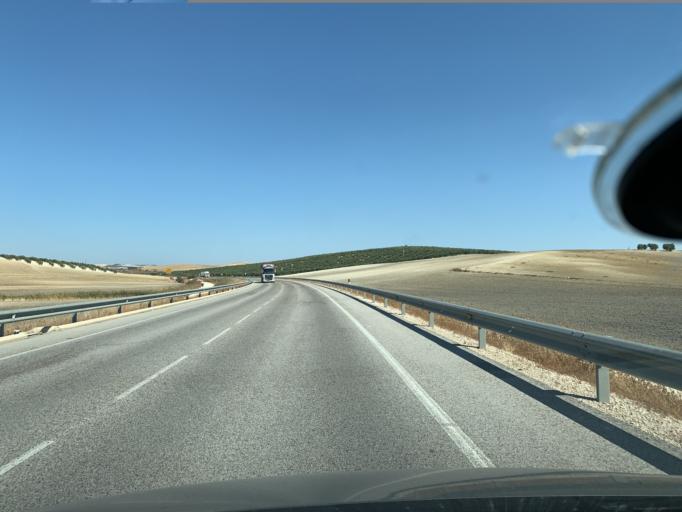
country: ES
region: Andalusia
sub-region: Provincia de Sevilla
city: Marchena
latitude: 37.3183
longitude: -5.3928
